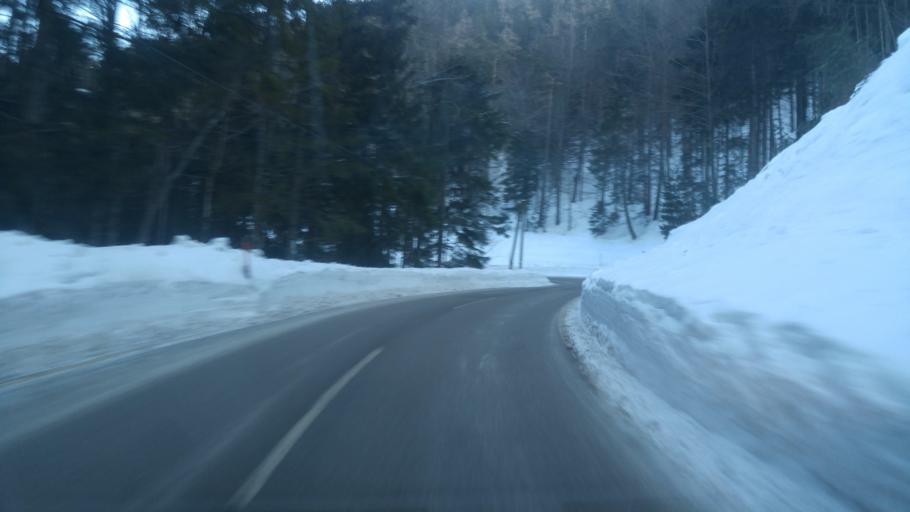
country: AT
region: Lower Austria
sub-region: Politischer Bezirk Lilienfeld
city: Hohenberg
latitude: 47.8780
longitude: 15.6302
